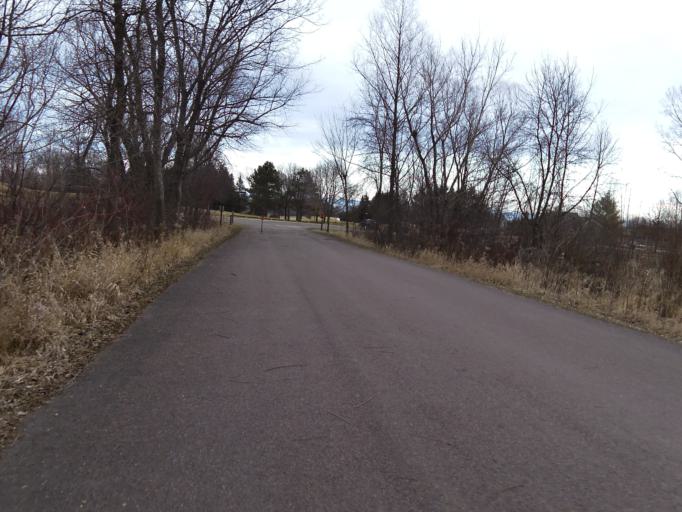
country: US
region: Minnesota
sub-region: Scott County
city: Prior Lake
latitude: 44.6888
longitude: -93.3887
